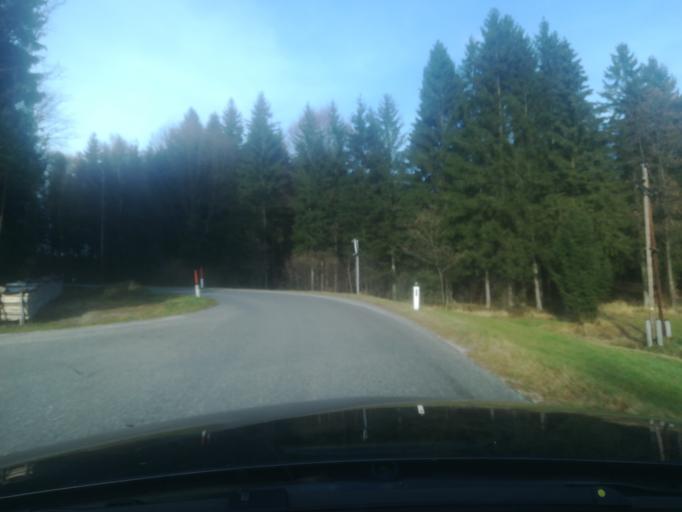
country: AT
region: Upper Austria
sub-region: Politischer Bezirk Perg
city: Perg
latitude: 48.3227
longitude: 14.6596
